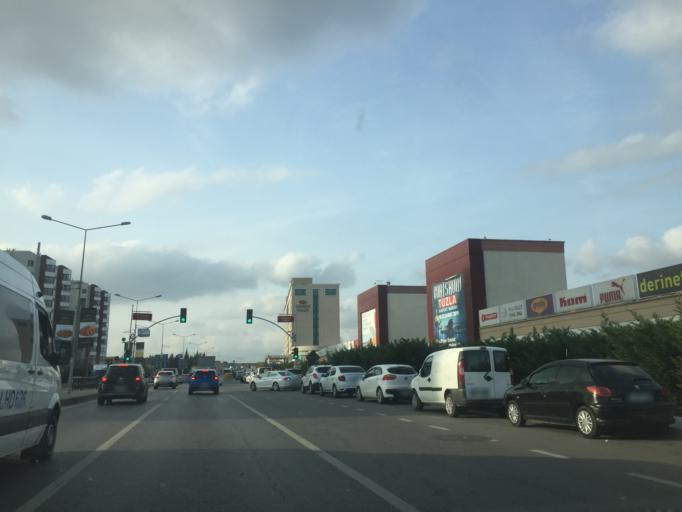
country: TR
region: Istanbul
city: Sultanbeyli
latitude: 40.9365
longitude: 29.3253
